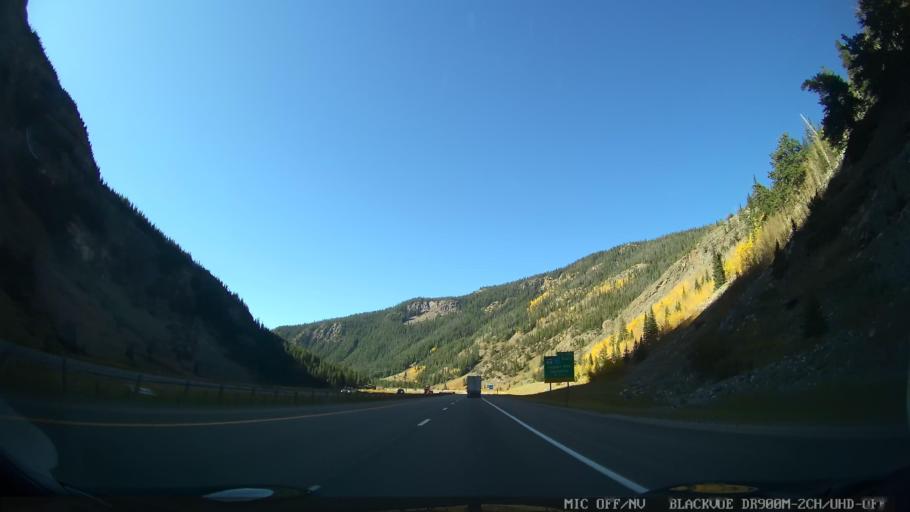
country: US
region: Colorado
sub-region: Summit County
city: Frisco
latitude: 39.5251
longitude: -106.1404
